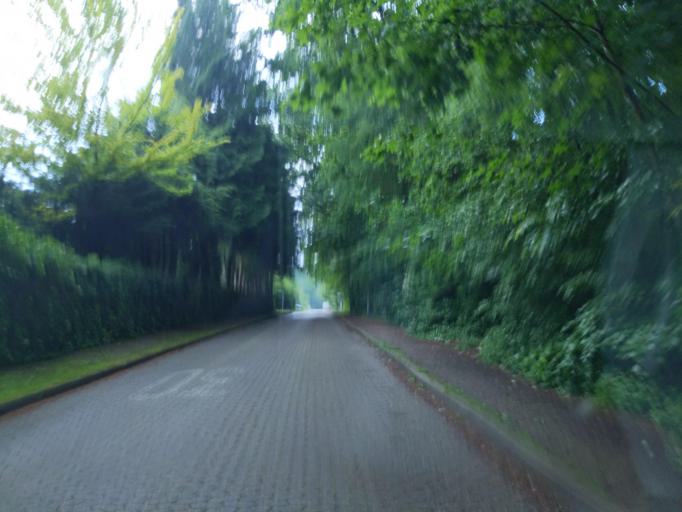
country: DE
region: Lower Saxony
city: Walsrode
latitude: 52.8726
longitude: 9.5937
